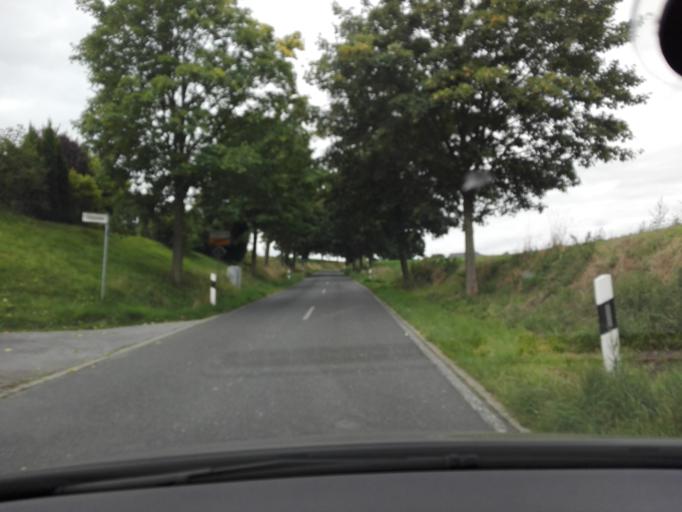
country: DE
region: North Rhine-Westphalia
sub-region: Regierungsbezirk Arnsberg
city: Frondenberg
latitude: 51.5152
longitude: 7.7688
